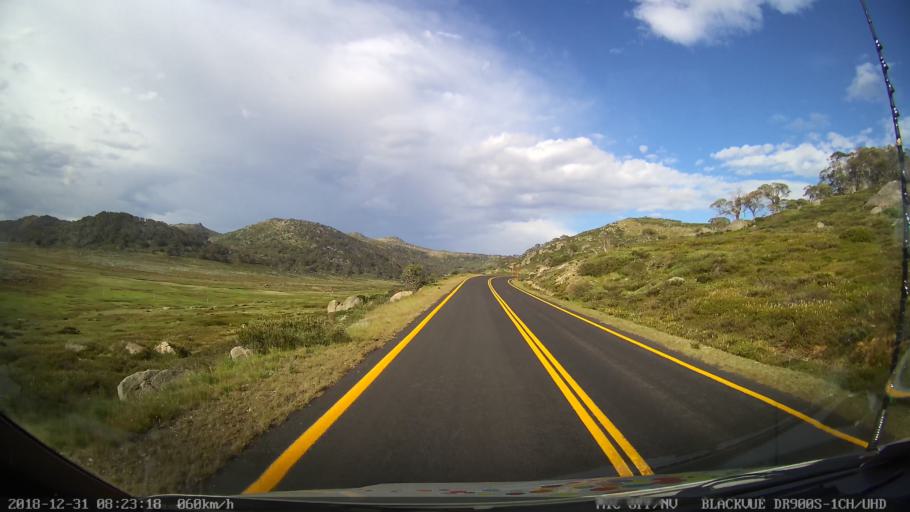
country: AU
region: New South Wales
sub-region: Snowy River
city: Jindabyne
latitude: -36.4277
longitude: 148.3506
